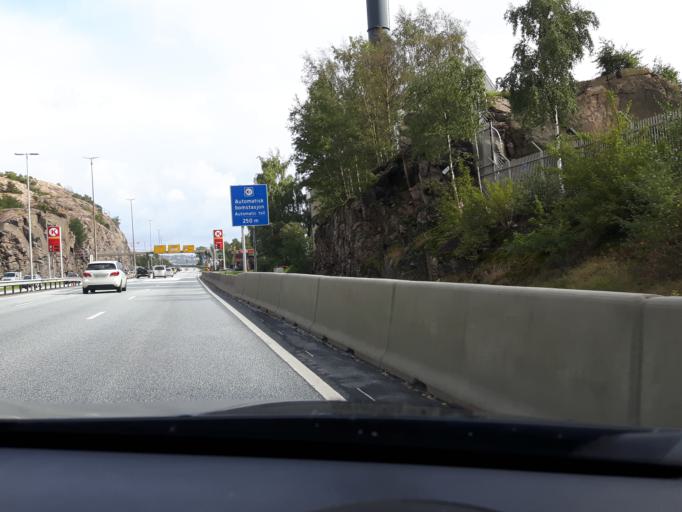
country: NO
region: Vest-Agder
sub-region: Kristiansand
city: Kristiansand
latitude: 58.1411
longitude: 7.9717
